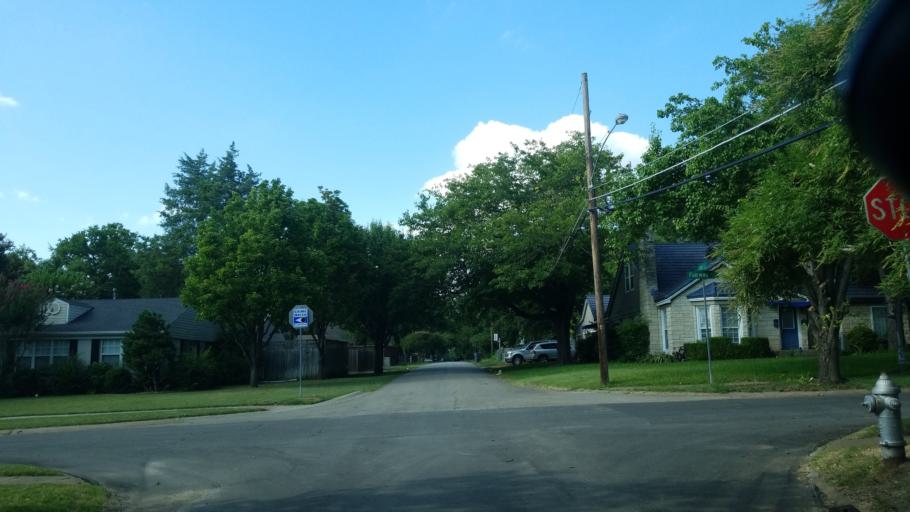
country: US
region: Texas
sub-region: Dallas County
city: Dallas
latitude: 32.7703
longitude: -96.7145
